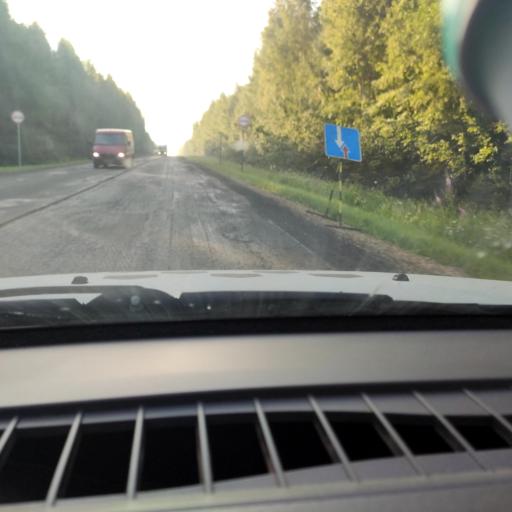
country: RU
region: Kirov
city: Omutninsk
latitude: 58.7649
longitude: 51.9867
